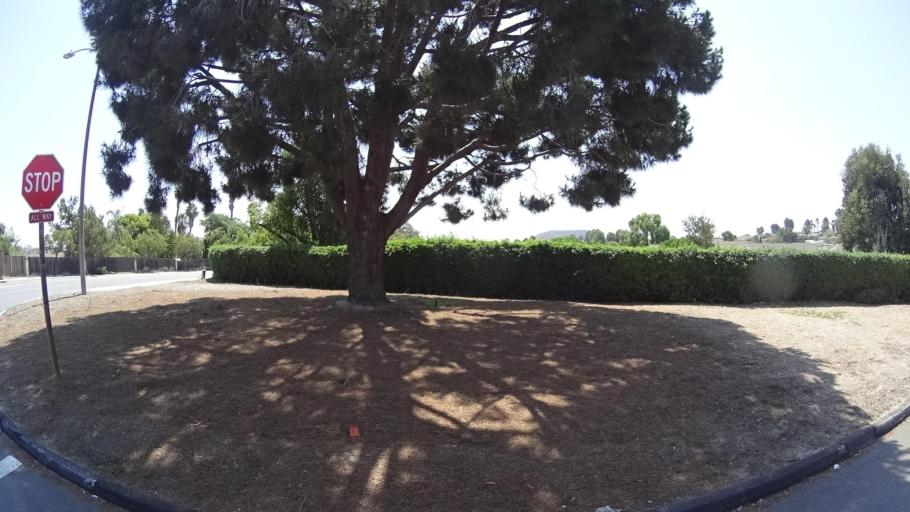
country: US
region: California
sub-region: San Diego County
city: Vista
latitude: 33.1830
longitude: -117.2732
